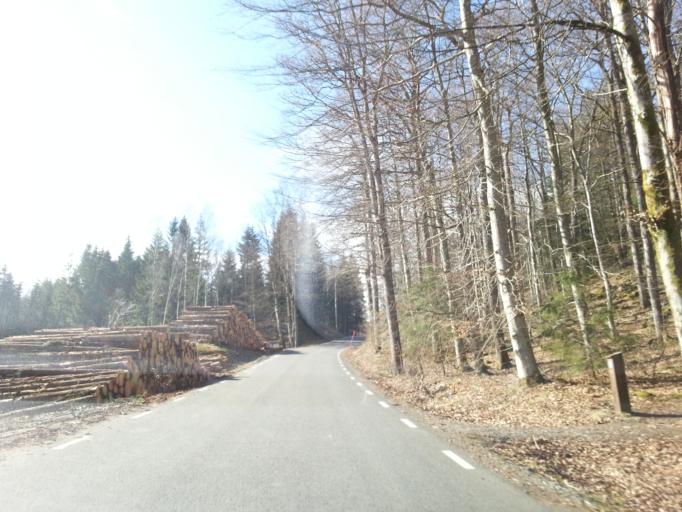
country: SE
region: Vaestra Goetaland
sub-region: Kungalvs Kommun
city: Diserod
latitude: 57.9620
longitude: 12.0078
